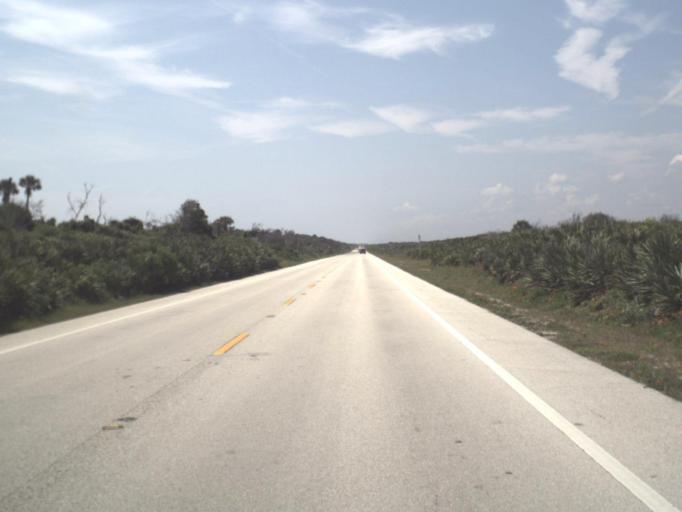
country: US
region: Florida
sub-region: Saint Johns County
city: Palm Valley
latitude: 30.0981
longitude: -81.3411
